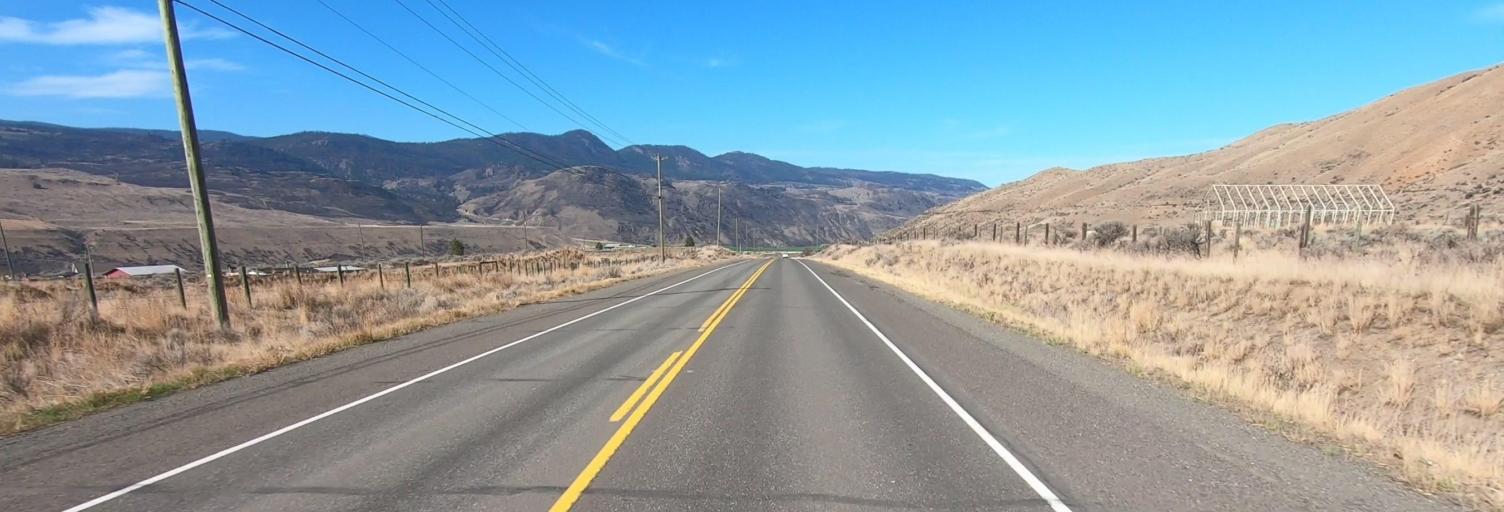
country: CA
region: British Columbia
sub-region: Thompson-Nicola Regional District
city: Ashcroft
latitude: 50.7647
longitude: -120.9867
